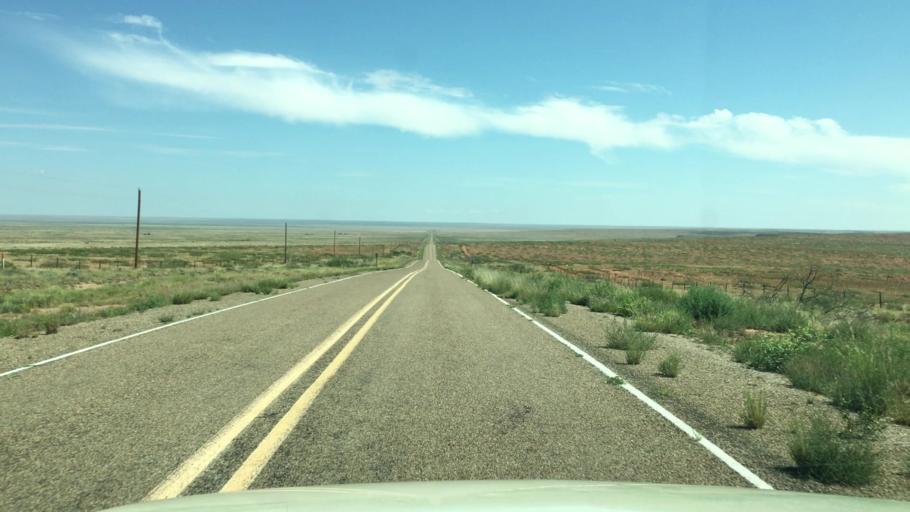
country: US
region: New Mexico
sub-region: Chaves County
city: Roswell
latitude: 33.9680
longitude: -104.5805
